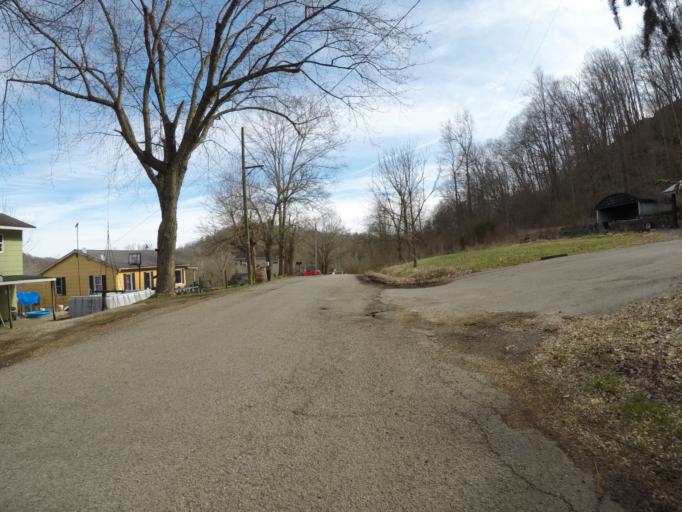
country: US
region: West Virginia
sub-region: Wayne County
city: Lavalette
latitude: 38.3402
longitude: -82.5050
